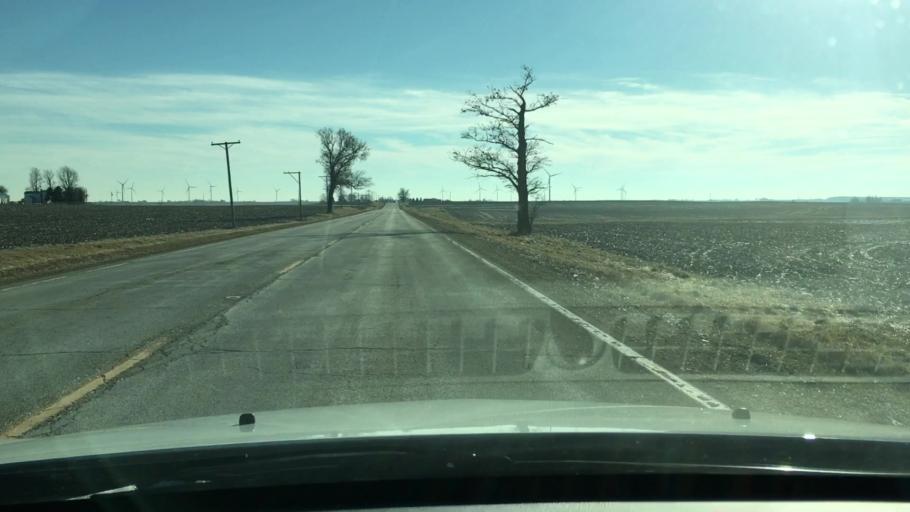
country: US
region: Illinois
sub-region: LaSalle County
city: Mendota
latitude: 41.6762
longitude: -89.1298
